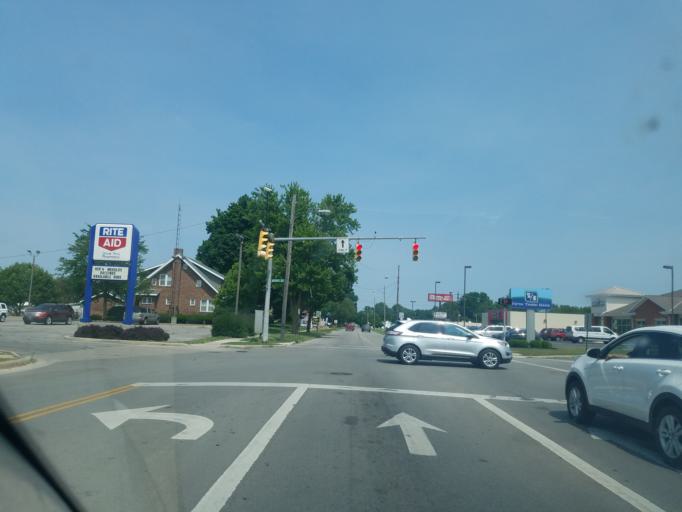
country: US
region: Ohio
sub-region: Seneca County
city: Tiffin
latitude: 41.1124
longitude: -83.1993
